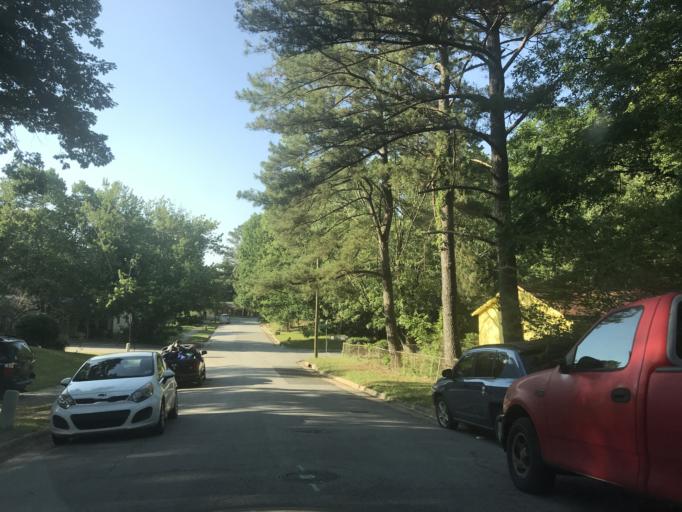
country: US
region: North Carolina
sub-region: Wake County
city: Garner
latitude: 35.7406
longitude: -78.6161
